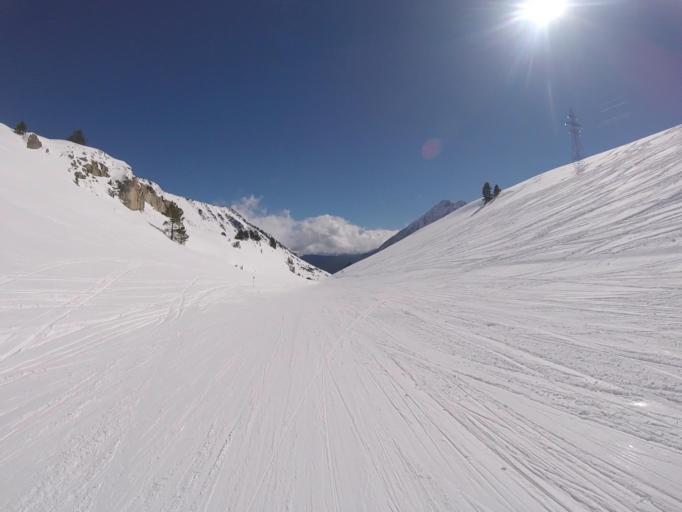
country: ES
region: Catalonia
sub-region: Provincia de Lleida
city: Espot
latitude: 42.6597
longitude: 0.9890
